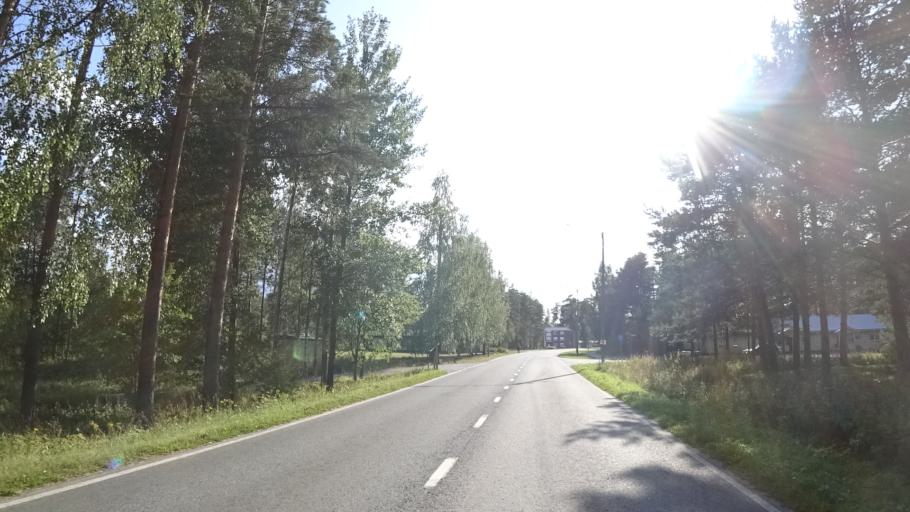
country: FI
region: North Karelia
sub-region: Keski-Karjala
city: Kesaelahti
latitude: 61.8923
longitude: 29.8424
